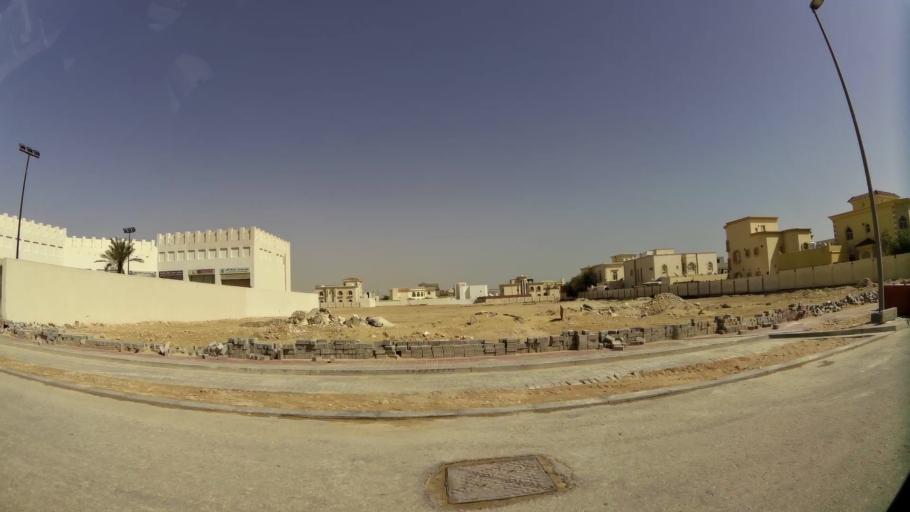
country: QA
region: Baladiyat ad Dawhah
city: Doha
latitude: 25.3606
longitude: 51.4971
